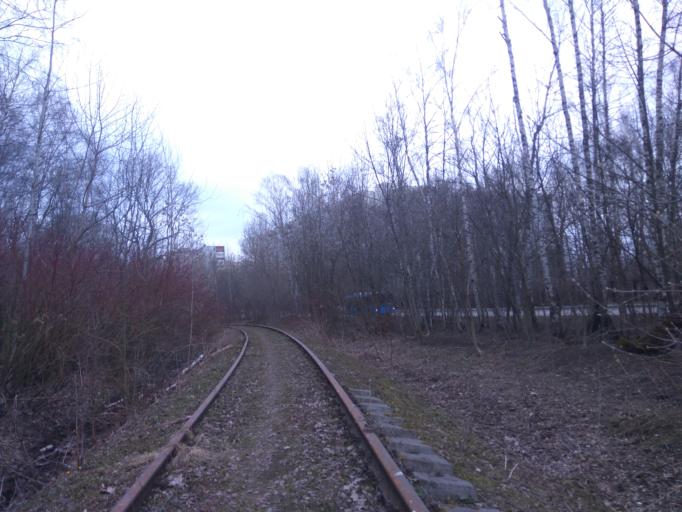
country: RU
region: Moscow
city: Vagonoremont
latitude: 55.8990
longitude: 37.5561
